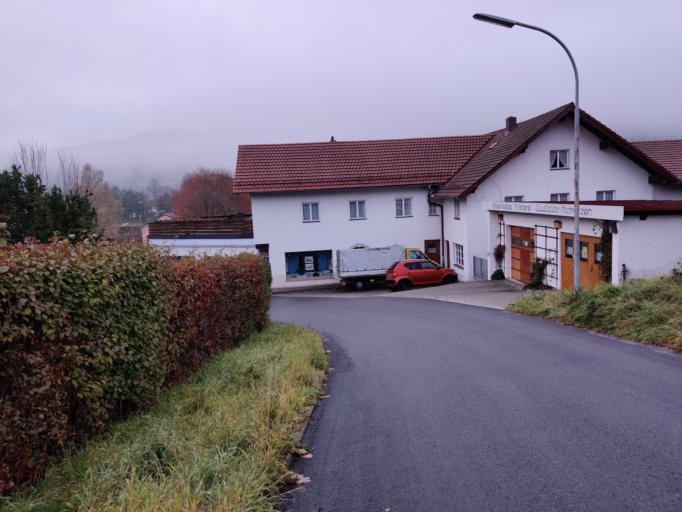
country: DE
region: Bavaria
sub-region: Upper Palatinate
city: Lam
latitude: 49.1940
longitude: 13.0534
